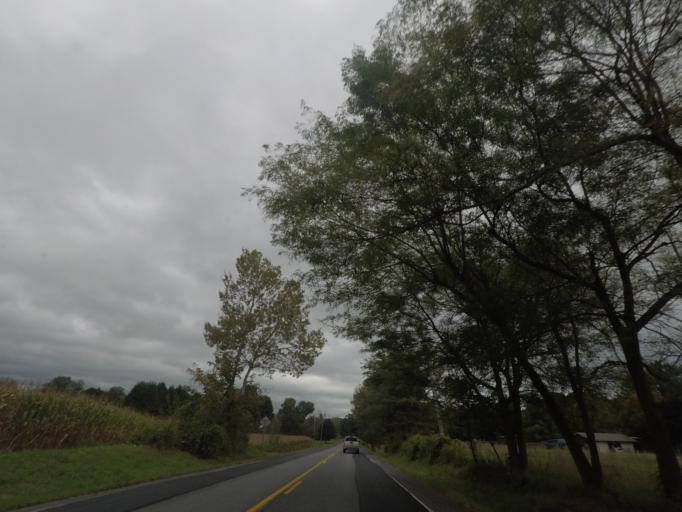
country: US
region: New York
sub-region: Rensselaer County
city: Hoosick Falls
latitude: 42.9519
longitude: -73.4111
